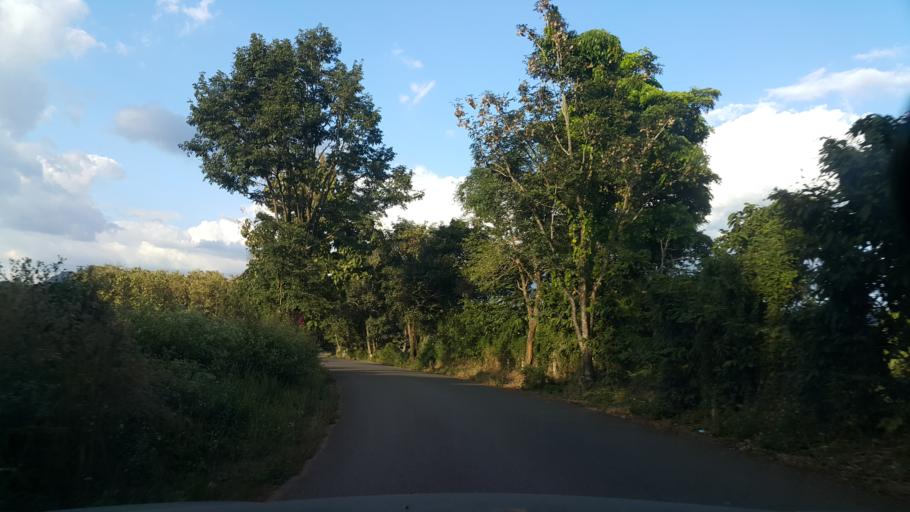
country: TH
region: Chiang Mai
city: Mae On
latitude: 18.7443
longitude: 99.2401
